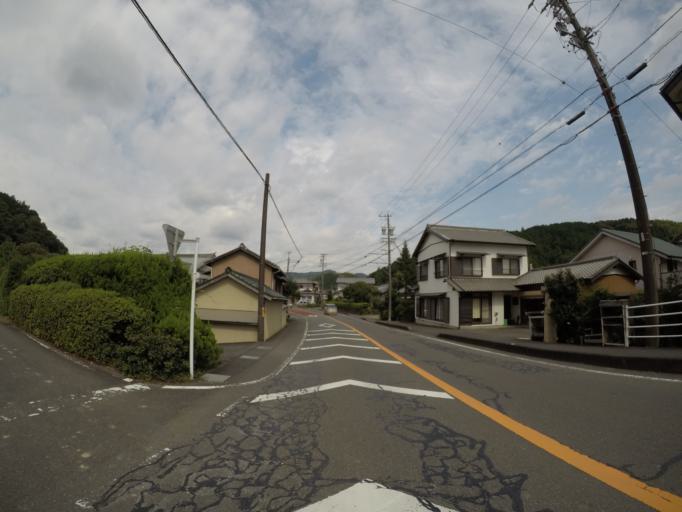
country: JP
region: Shizuoka
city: Shimada
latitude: 34.8507
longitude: 138.1832
